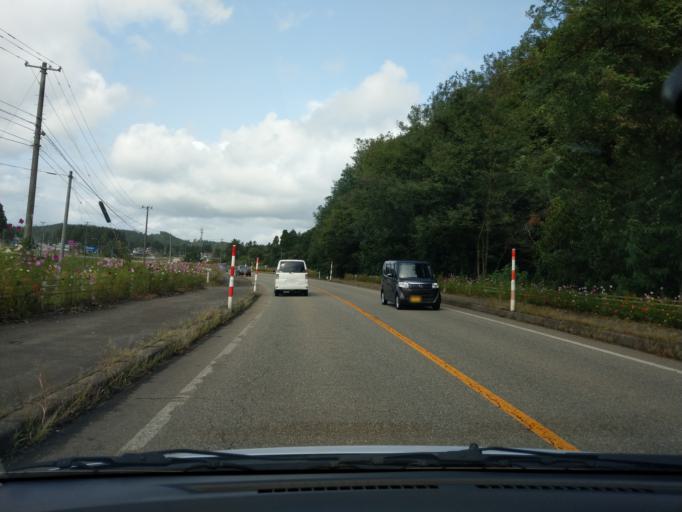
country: JP
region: Akita
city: Omagari
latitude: 39.4360
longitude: 140.3682
